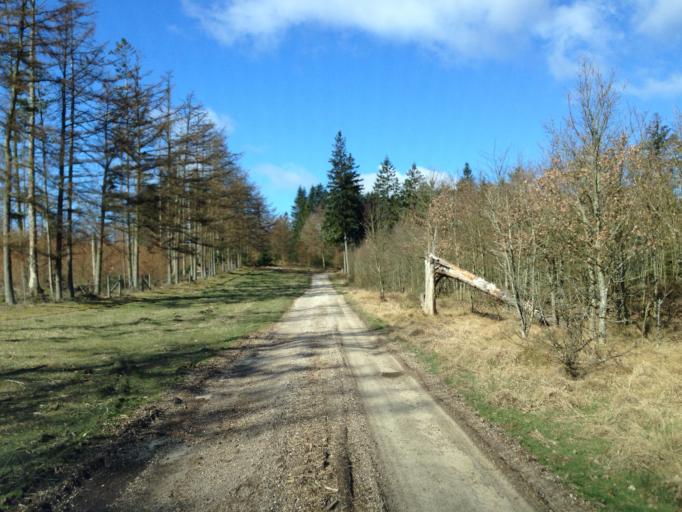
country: DK
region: Central Jutland
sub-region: Holstebro Kommune
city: Ulfborg
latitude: 56.2648
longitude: 8.4652
